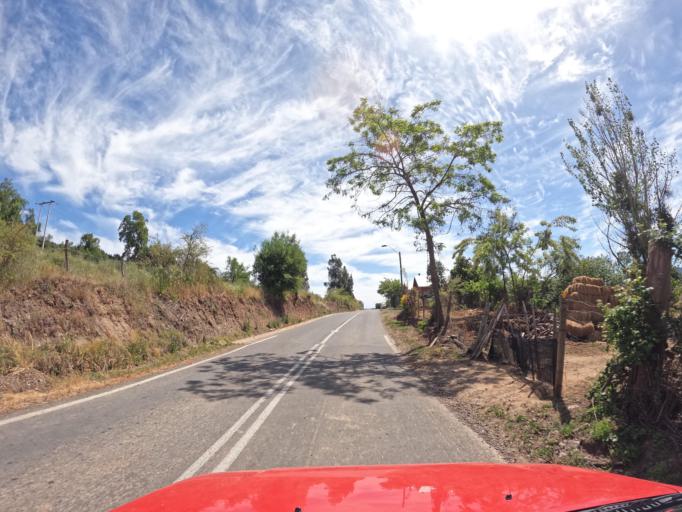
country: CL
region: Maule
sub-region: Provincia de Talca
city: Talca
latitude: -34.9896
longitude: -71.8384
